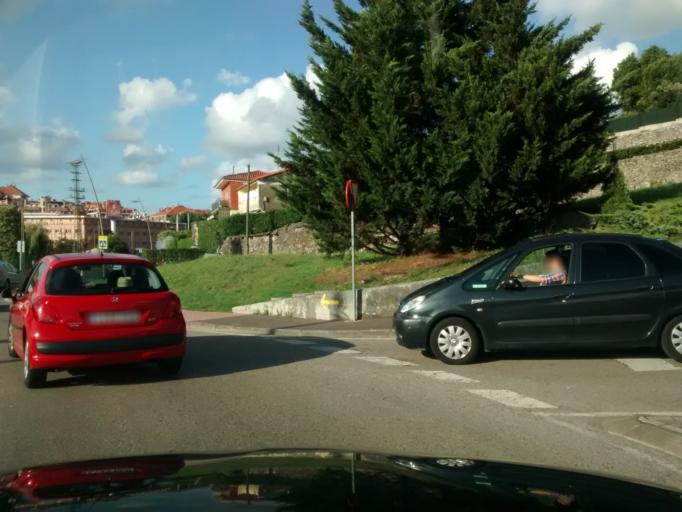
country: ES
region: Cantabria
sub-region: Provincia de Cantabria
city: Castro-Urdiales
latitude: 43.3673
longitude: -3.2167
